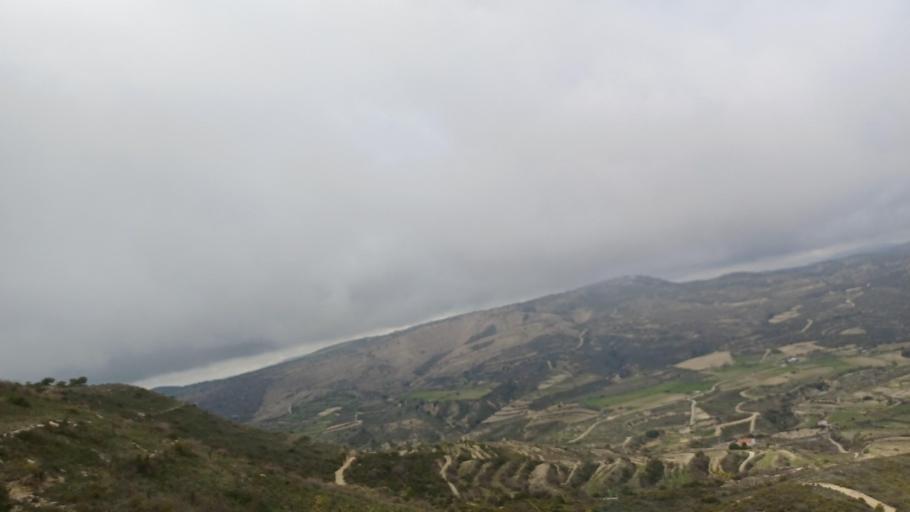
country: CY
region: Limassol
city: Pachna
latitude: 34.7677
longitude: 32.8261
